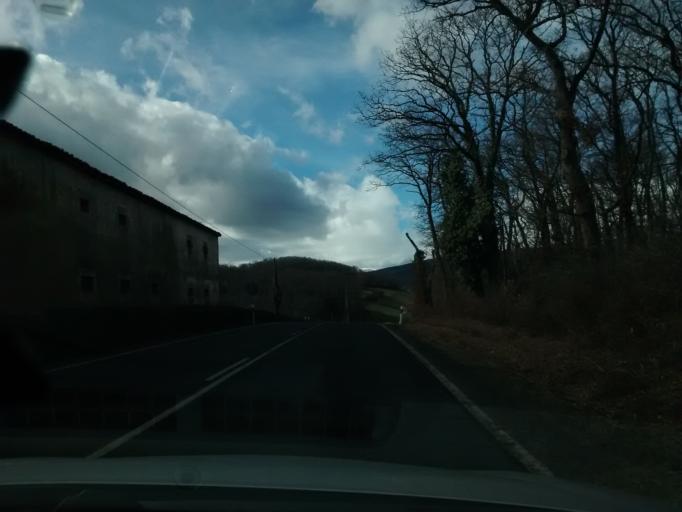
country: ES
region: Castille and Leon
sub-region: Provincia de Burgos
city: Espinosa de los Monteros
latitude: 43.0702
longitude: -3.5229
